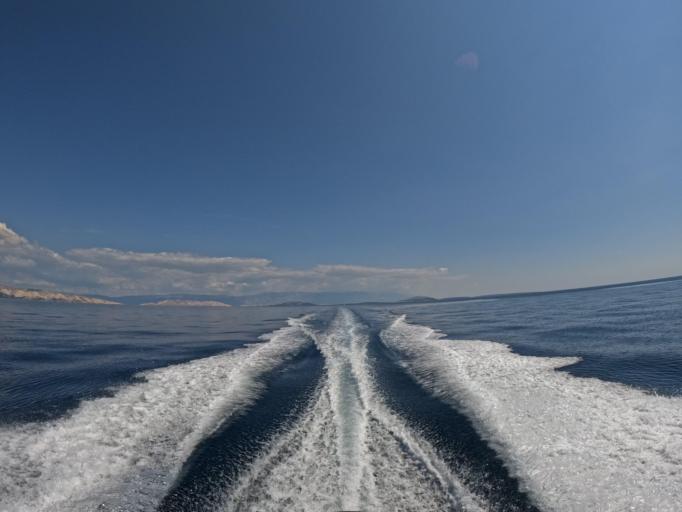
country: HR
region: Primorsko-Goranska
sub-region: Grad Krk
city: Krk
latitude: 44.9149
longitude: 14.5768
